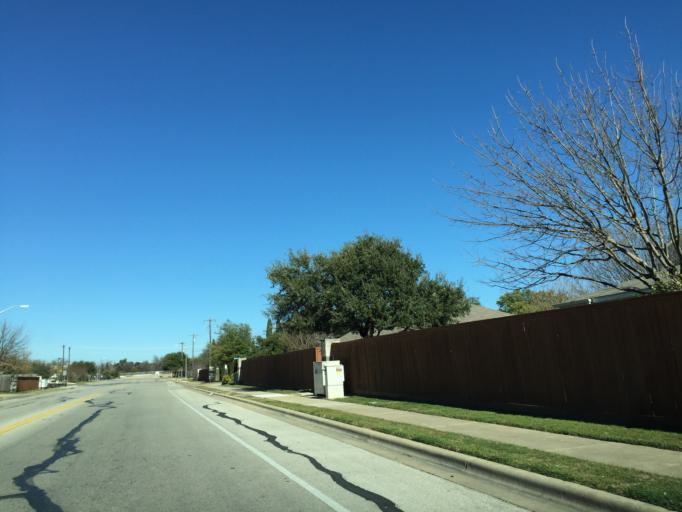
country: US
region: Texas
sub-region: Williamson County
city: Leander
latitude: 30.5567
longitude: -97.8405
